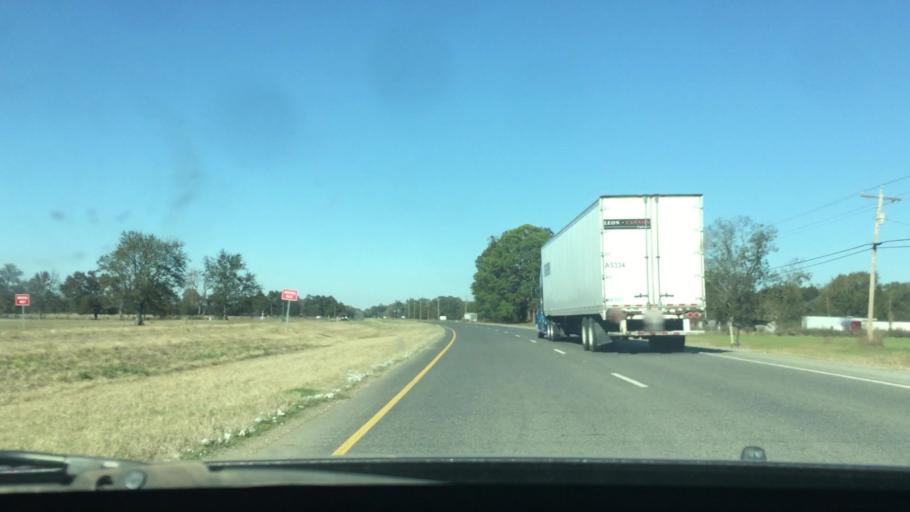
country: US
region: Louisiana
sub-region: Richland Parish
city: Rayville
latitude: 32.3779
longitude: -91.7696
